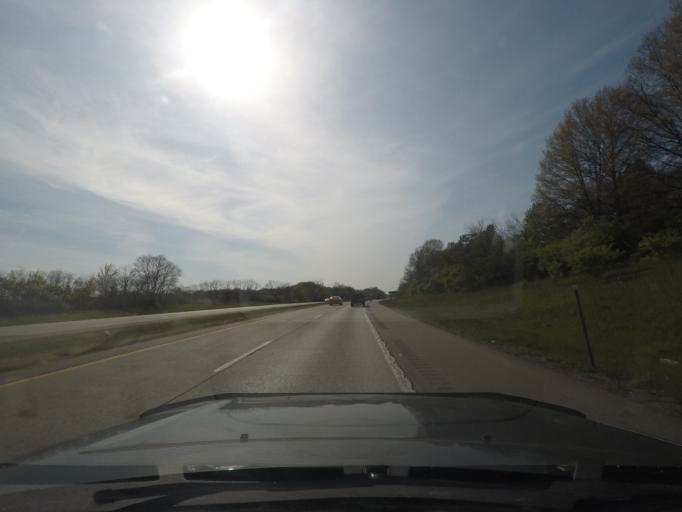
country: US
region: Michigan
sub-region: Berrien County
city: Niles
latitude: 41.8016
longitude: -86.2806
